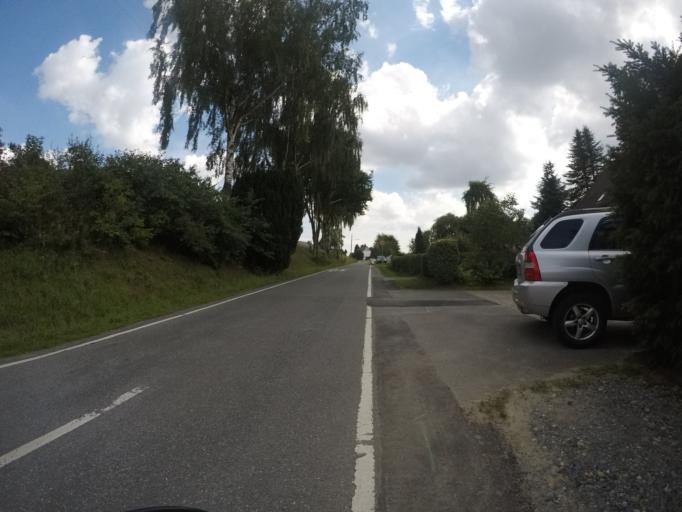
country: DE
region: North Rhine-Westphalia
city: Enger
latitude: 52.1055
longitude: 8.5861
